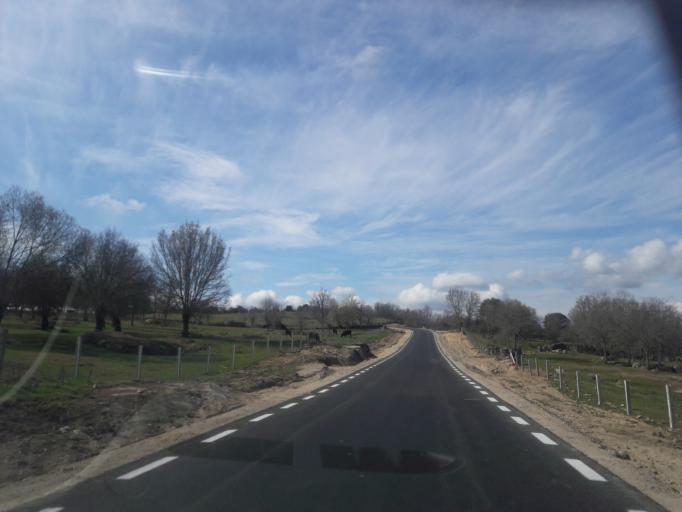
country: ES
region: Castille and Leon
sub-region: Provincia de Salamanca
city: Monleon
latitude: 40.5299
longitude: -5.8332
